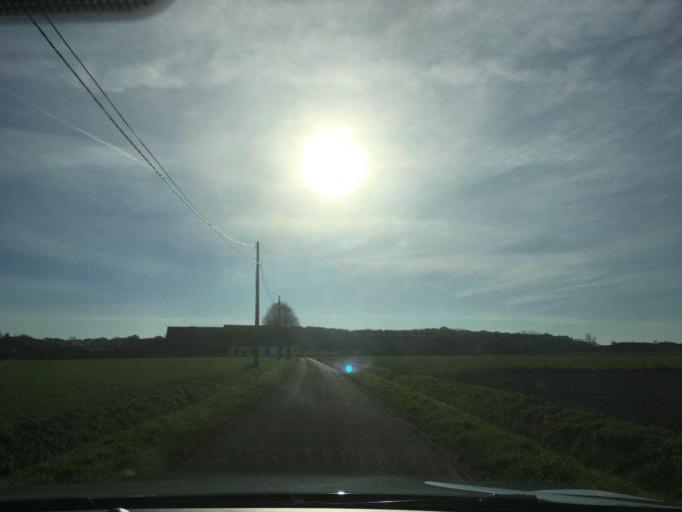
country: BE
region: Flanders
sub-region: Provincie West-Vlaanderen
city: Pittem
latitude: 50.9725
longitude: 3.2400
